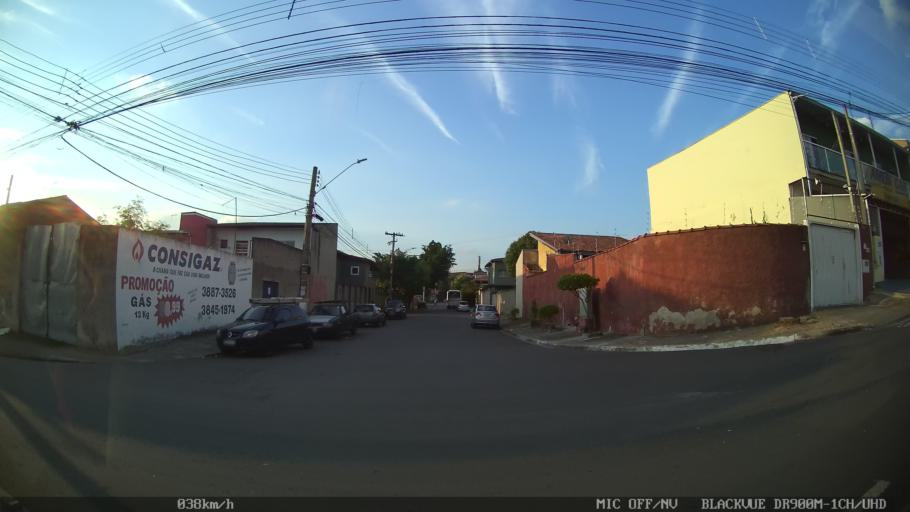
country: BR
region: Sao Paulo
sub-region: Hortolandia
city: Hortolandia
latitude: -22.8816
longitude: -47.1692
